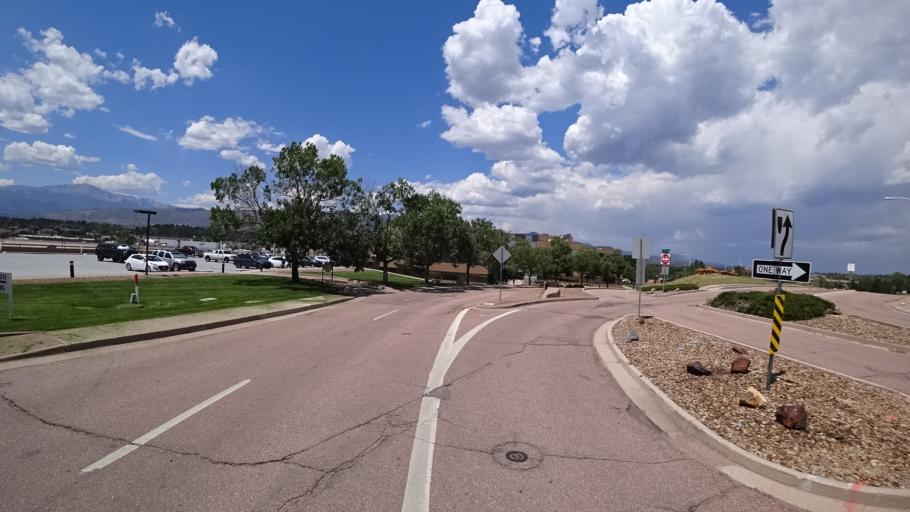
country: US
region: Colorado
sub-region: El Paso County
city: Air Force Academy
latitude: 38.9345
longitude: -104.8103
